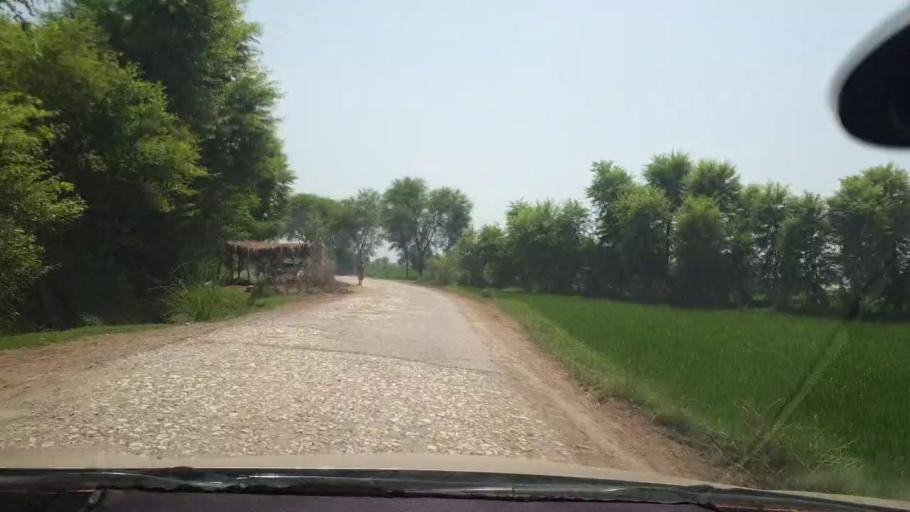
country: PK
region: Sindh
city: Kambar
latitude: 27.6669
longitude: 67.9436
